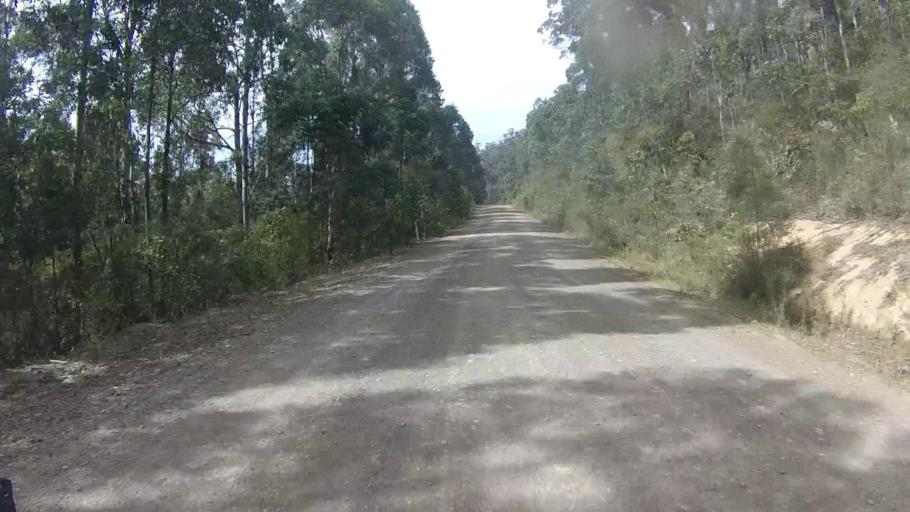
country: AU
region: Tasmania
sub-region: Sorell
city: Sorell
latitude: -42.7618
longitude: 147.8298
